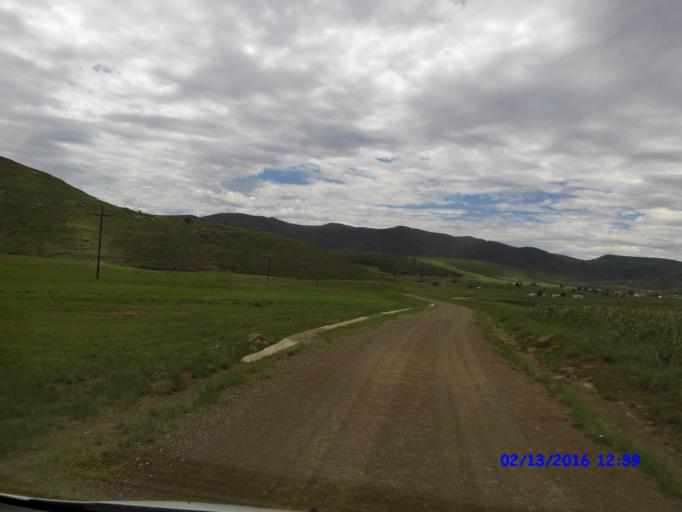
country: LS
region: Maseru
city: Nako
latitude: -29.8342
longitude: 28.0283
